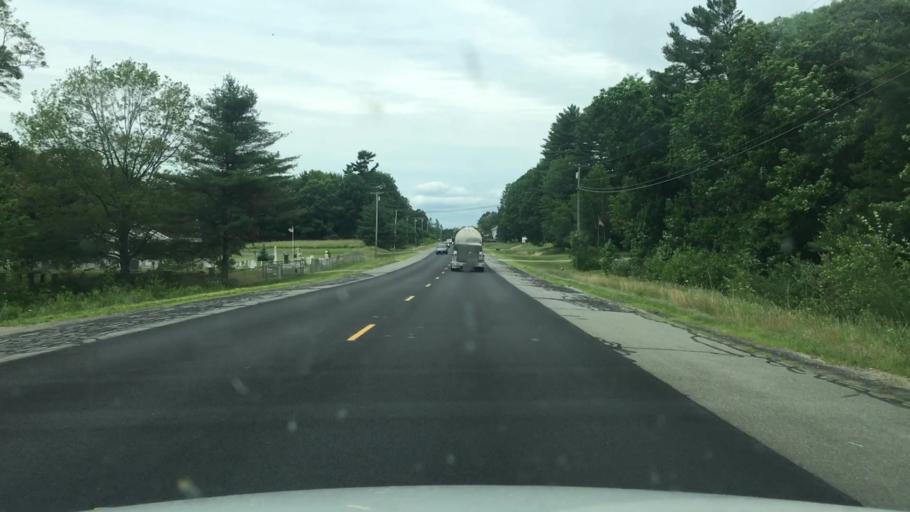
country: US
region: Maine
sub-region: Waldo County
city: Palermo
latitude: 44.3791
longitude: -69.4531
